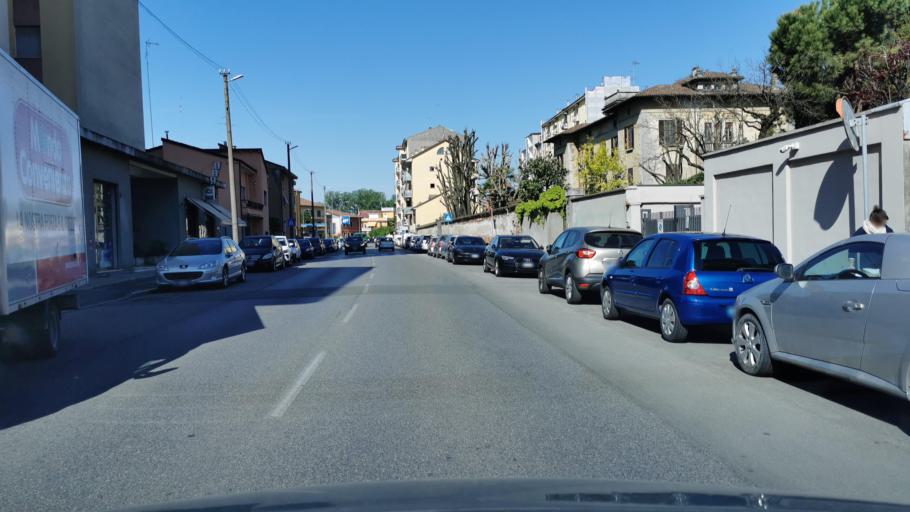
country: IT
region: Lombardy
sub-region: Provincia di Cremona
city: Cremona
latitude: 45.1292
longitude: 10.0241
